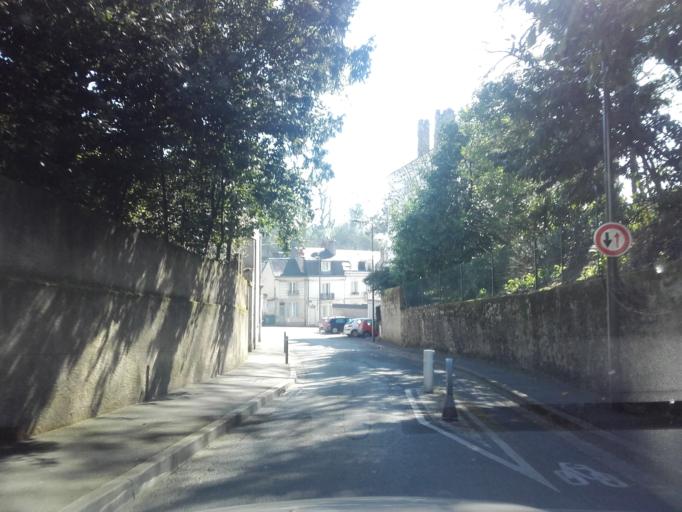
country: FR
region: Centre
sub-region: Departement d'Indre-et-Loire
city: Tours
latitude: 47.4048
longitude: 0.6942
